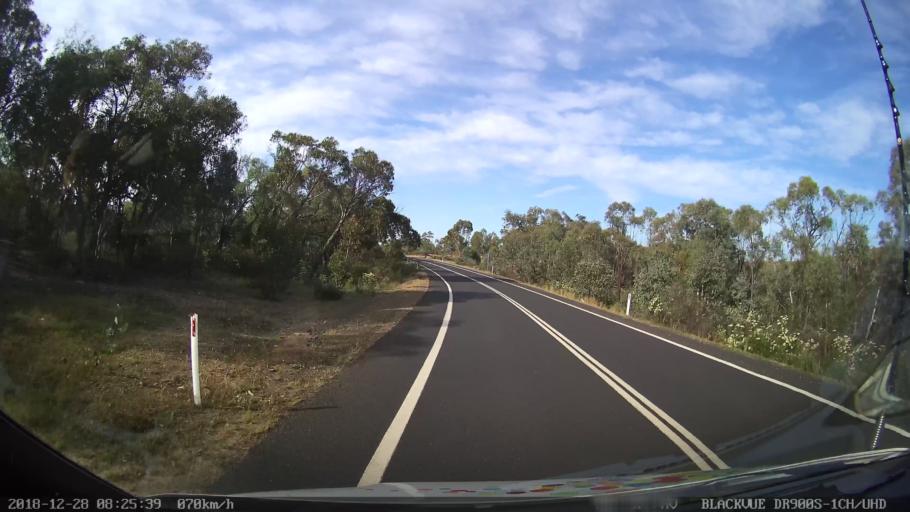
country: AU
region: New South Wales
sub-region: Blayney
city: Blayney
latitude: -33.9281
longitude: 149.3511
